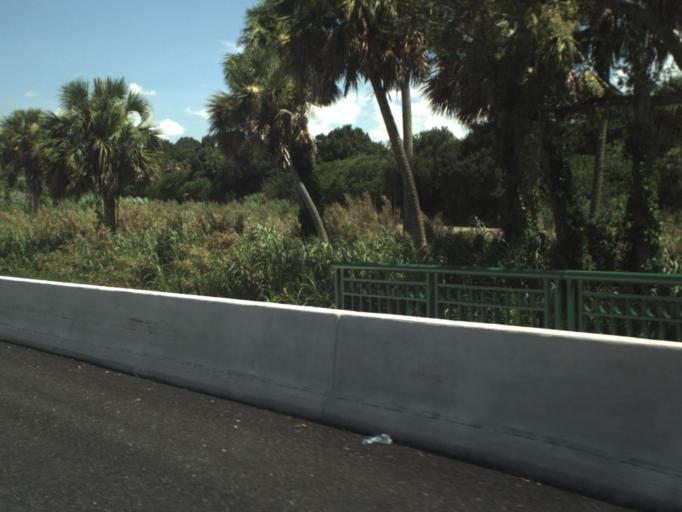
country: US
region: Florida
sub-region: Martin County
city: Indiantown
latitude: 27.0098
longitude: -80.4517
